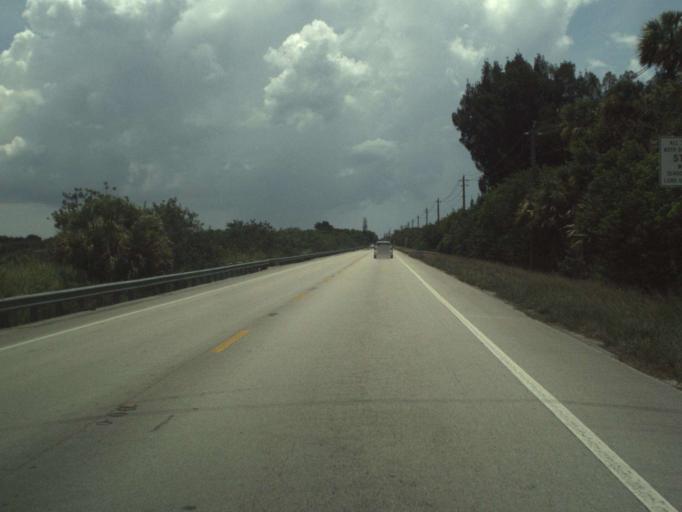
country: US
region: Florida
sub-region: Saint Lucie County
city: Lakewood Park
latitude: 27.5213
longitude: -80.4286
